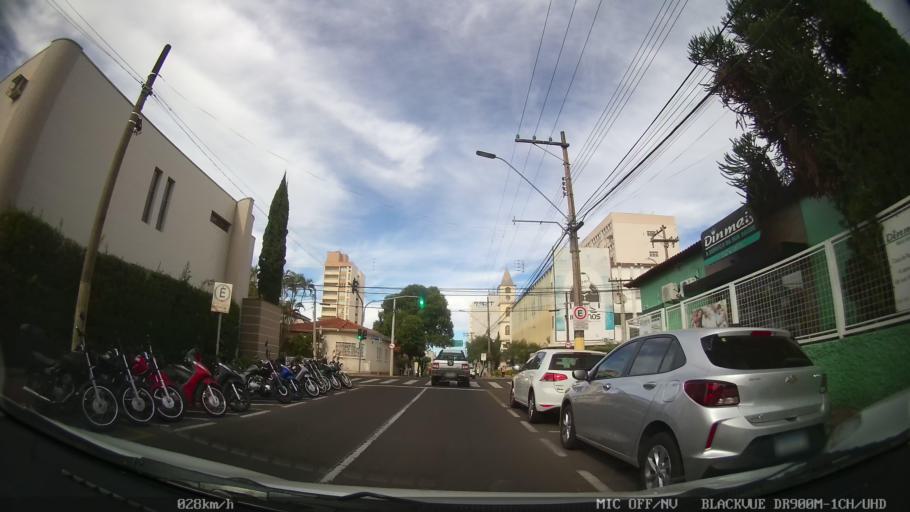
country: BR
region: Sao Paulo
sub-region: Catanduva
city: Catanduva
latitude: -21.1408
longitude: -48.9752
